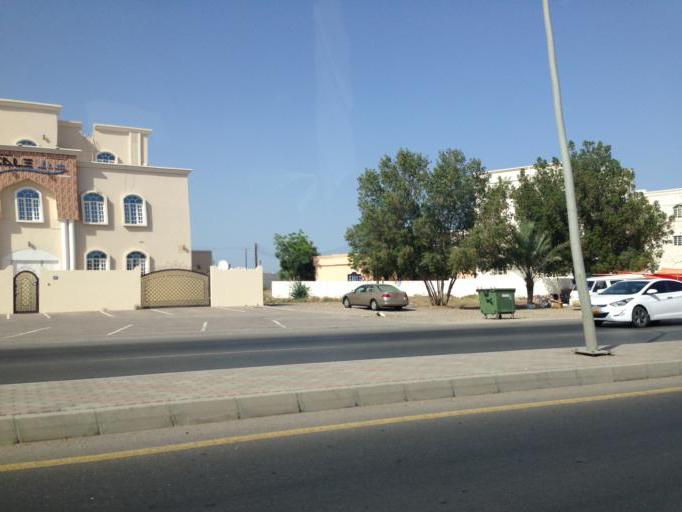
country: OM
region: Muhafazat Masqat
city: As Sib al Jadidah
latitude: 23.6121
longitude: 58.2378
